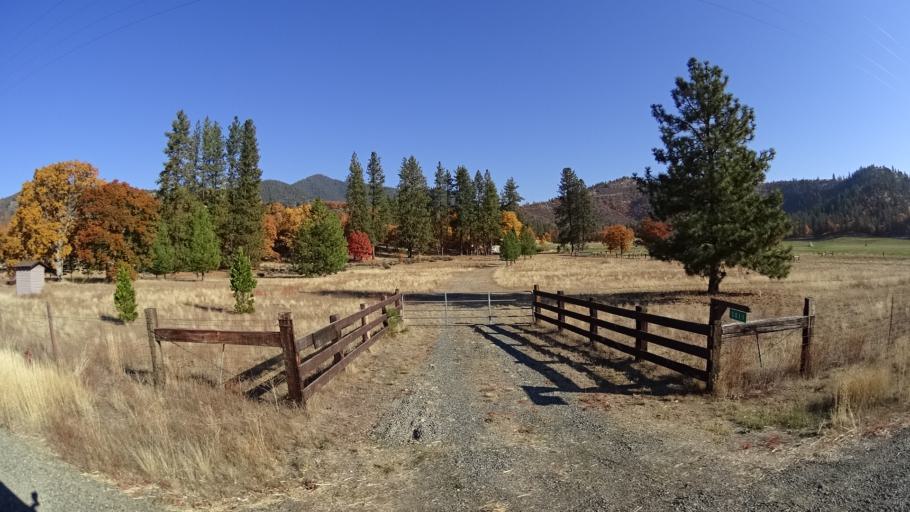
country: US
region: California
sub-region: Siskiyou County
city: Yreka
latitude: 41.6406
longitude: -122.9176
